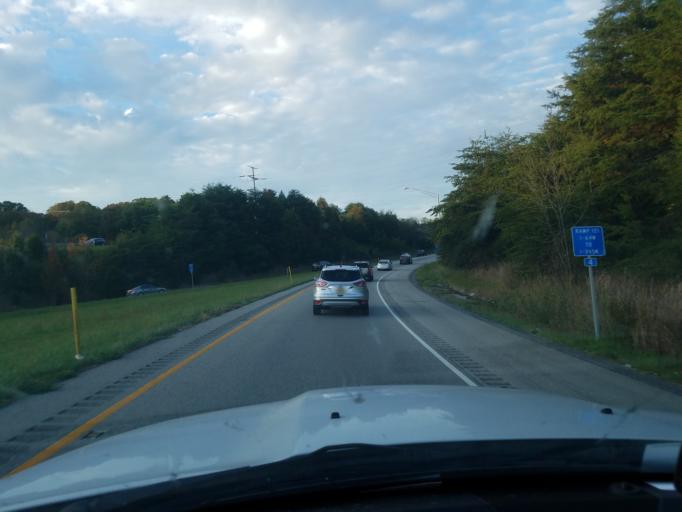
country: US
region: Indiana
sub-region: Floyd County
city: New Albany
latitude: 38.3027
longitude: -85.8497
